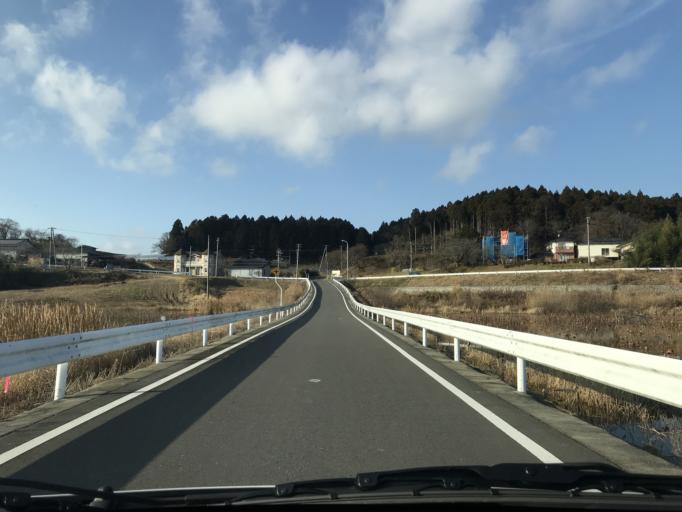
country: JP
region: Miyagi
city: Wakuya
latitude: 38.6826
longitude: 141.1149
